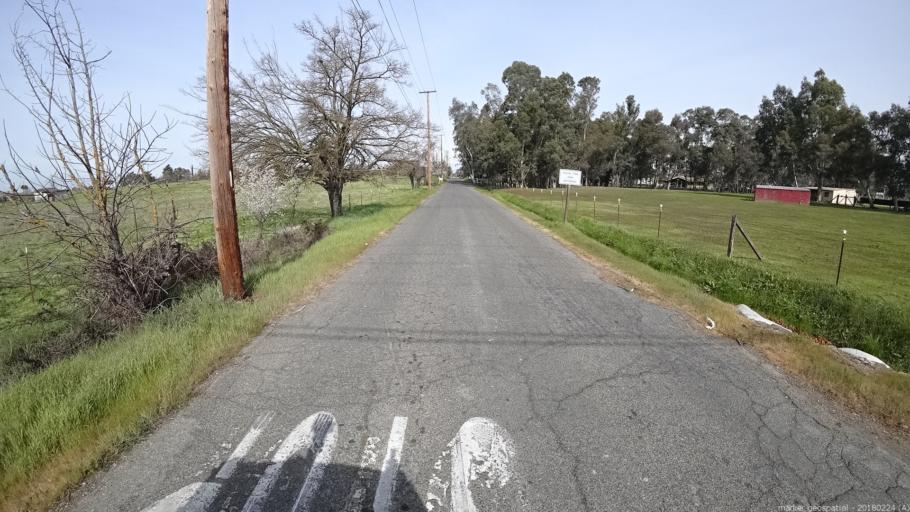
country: US
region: California
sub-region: Sacramento County
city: Rio Linda
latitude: 38.6915
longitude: -121.4708
